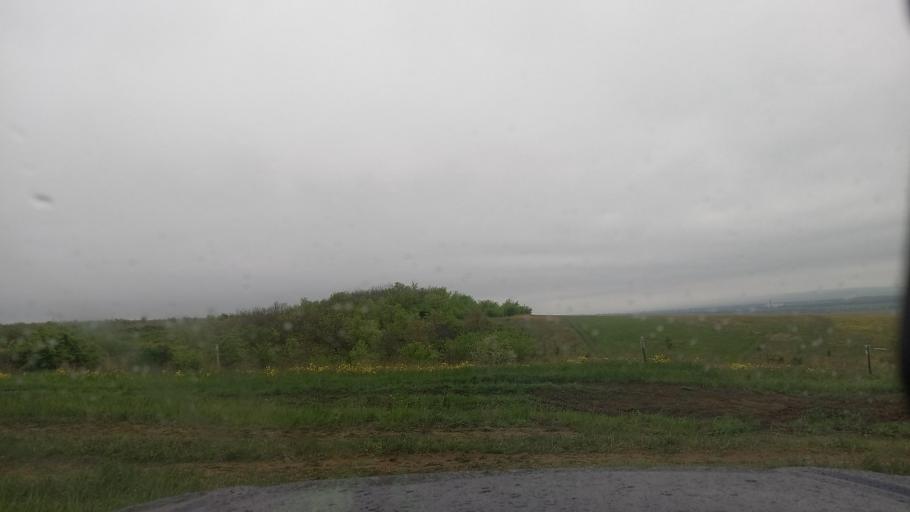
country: RU
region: Stavropol'skiy
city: Kursavka
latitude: 44.5100
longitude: 42.4313
